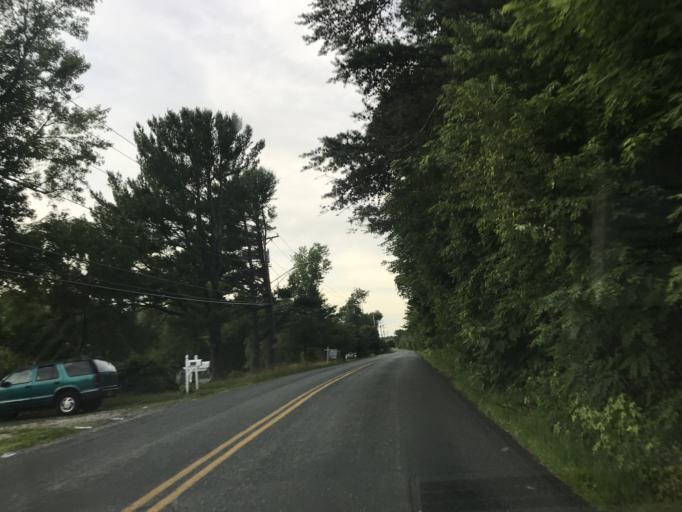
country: US
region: Maryland
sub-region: Harford County
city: Perryman
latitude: 39.4930
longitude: -76.2110
